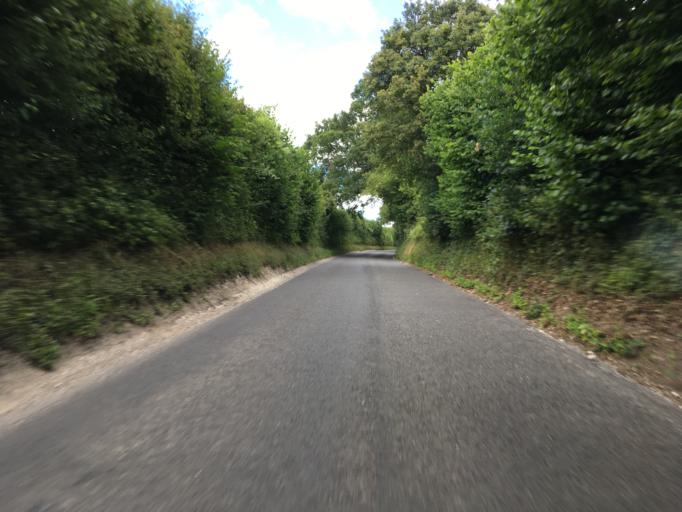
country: GB
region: England
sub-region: Hampshire
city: Overton
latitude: 51.2389
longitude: -1.3507
